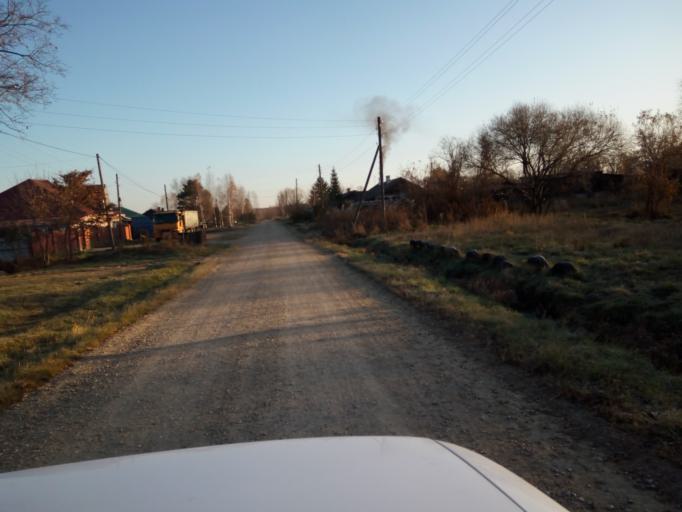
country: RU
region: Primorskiy
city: Lazo
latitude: 45.8798
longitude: 133.6530
